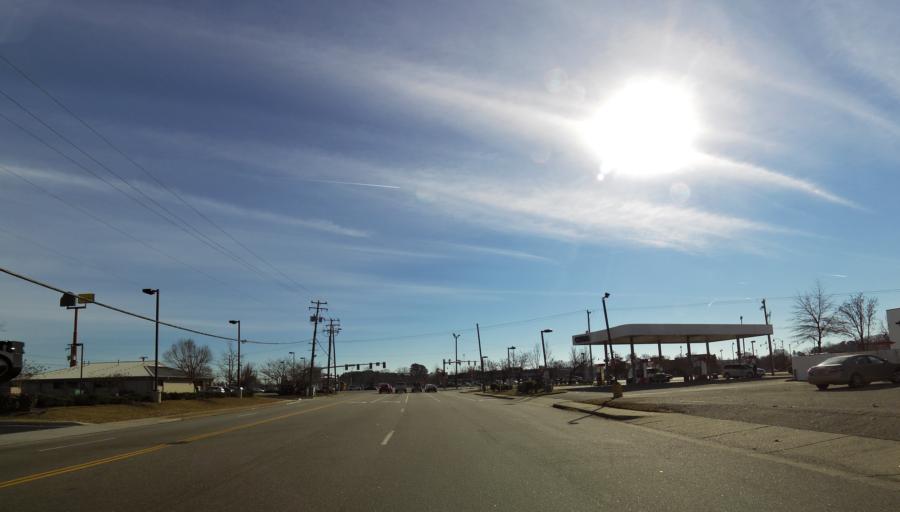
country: US
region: Virginia
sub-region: City of Hampton
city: Hampton
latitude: 37.0397
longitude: -76.4029
